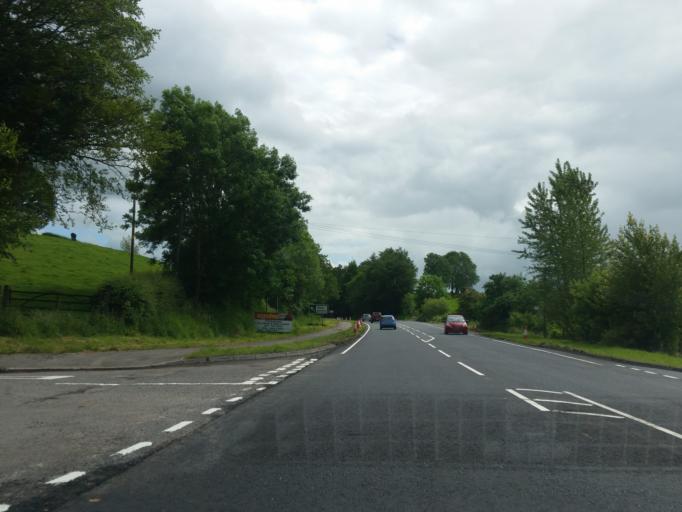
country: IE
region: Ulster
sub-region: County Monaghan
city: Monaghan
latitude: 54.4683
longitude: -7.0476
